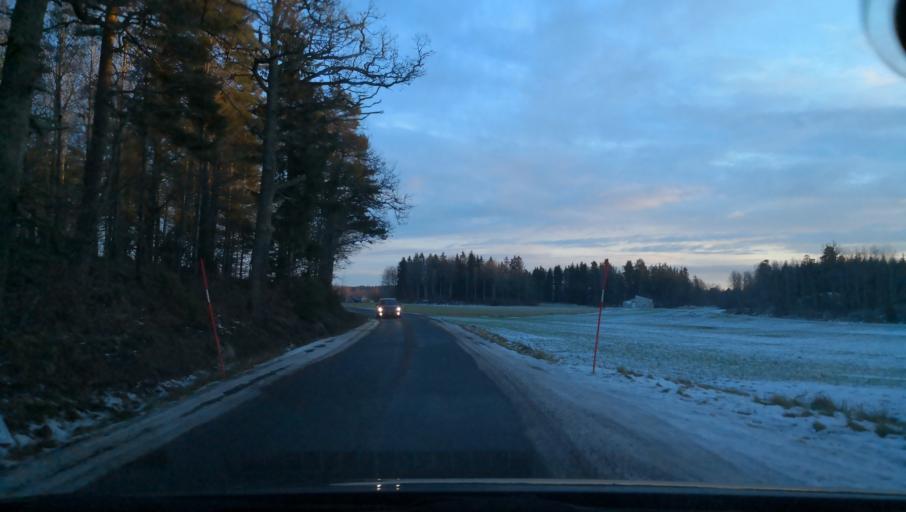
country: SE
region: Soedermanland
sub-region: Eskilstuna Kommun
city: Skogstorp
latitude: 59.2326
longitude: 16.3327
